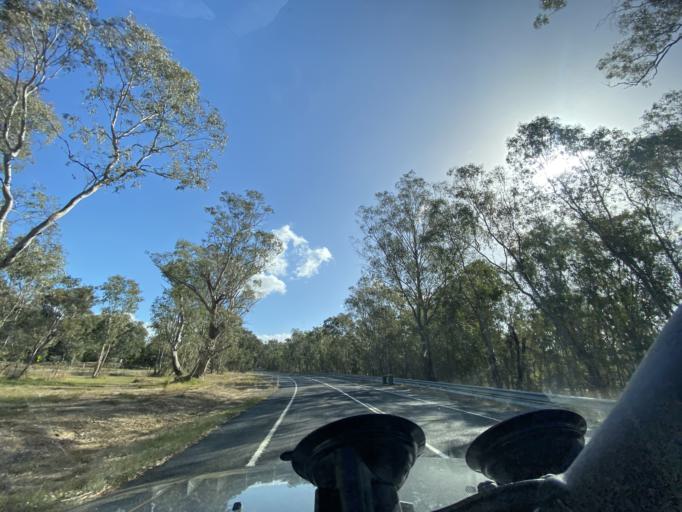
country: AU
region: Victoria
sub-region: Murrindindi
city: Kinglake West
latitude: -37.2474
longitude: 145.3750
